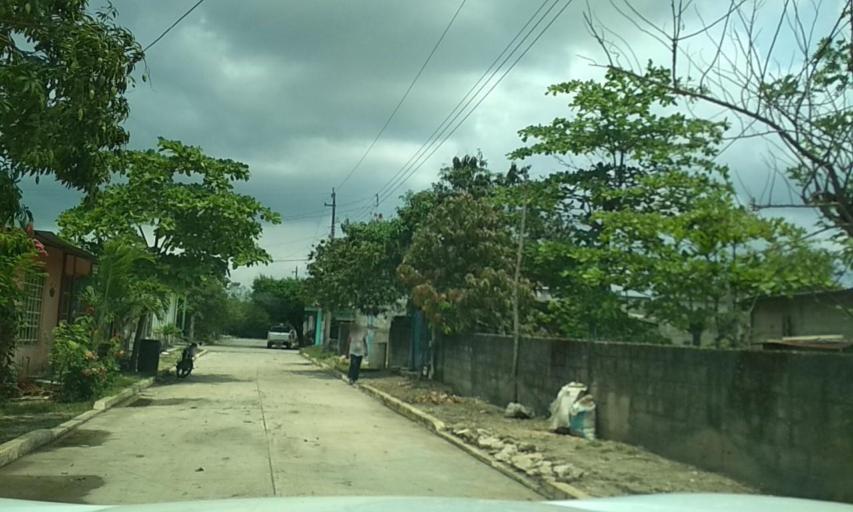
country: MX
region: Veracruz
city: Las Choapas
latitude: 17.8934
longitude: -94.0971
